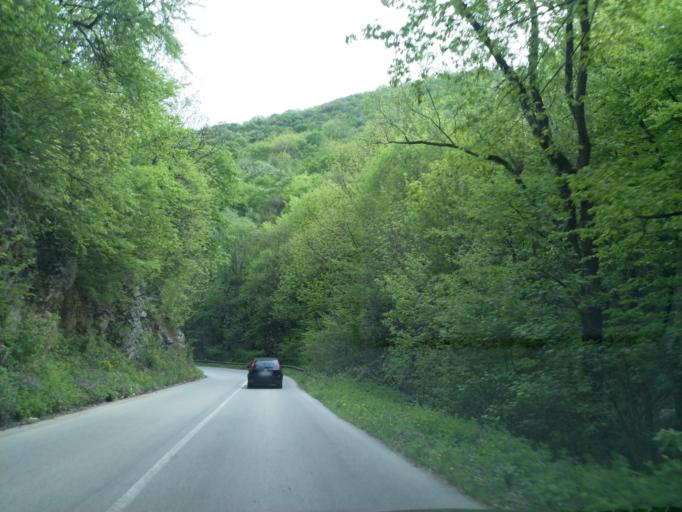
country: RS
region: Central Serbia
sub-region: Pomoravski Okrug
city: Despotovac
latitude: 43.9692
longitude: 21.5248
